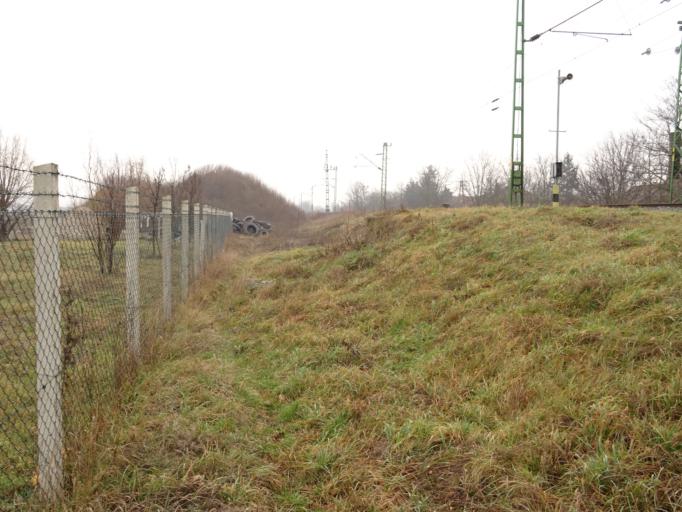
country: HU
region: Gyor-Moson-Sopron
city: Kony
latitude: 47.6341
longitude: 17.3637
